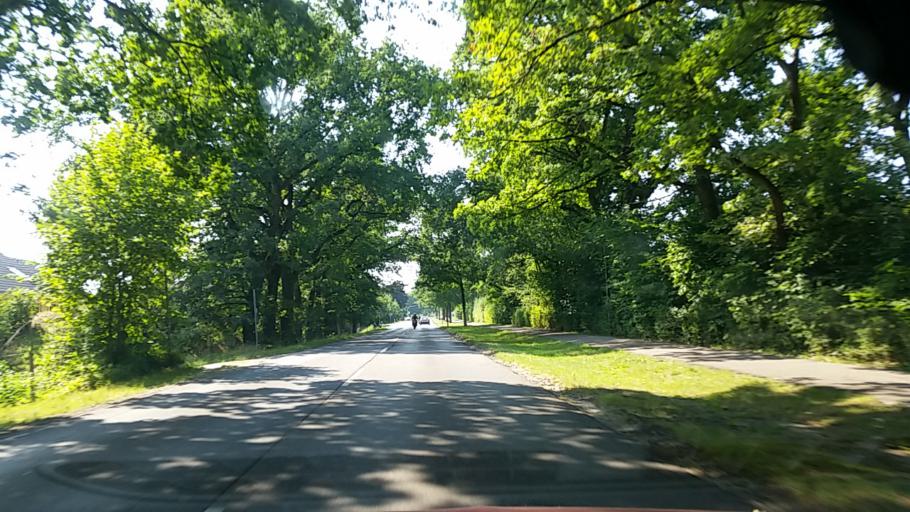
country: DE
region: Schleswig-Holstein
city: Glinde
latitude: 53.5407
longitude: 10.1930
